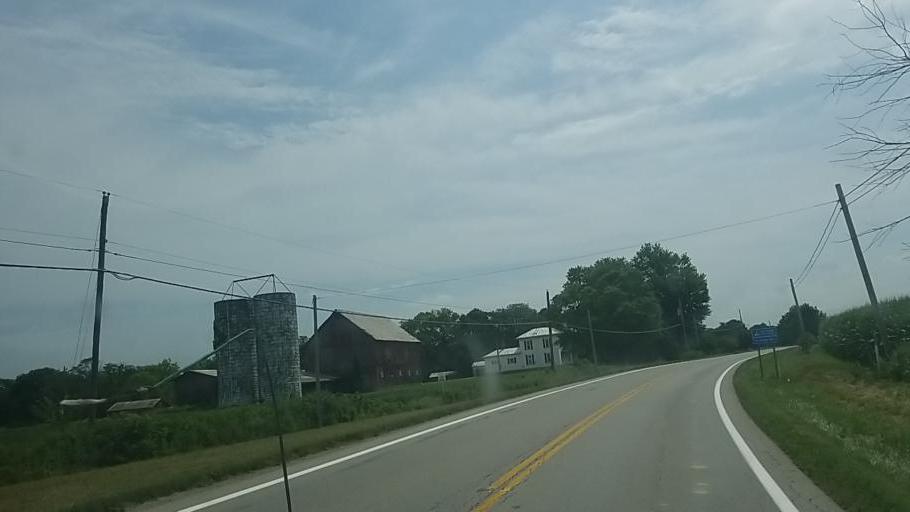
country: US
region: Ohio
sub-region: Delaware County
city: Sunbury
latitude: 40.2336
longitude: -82.8369
